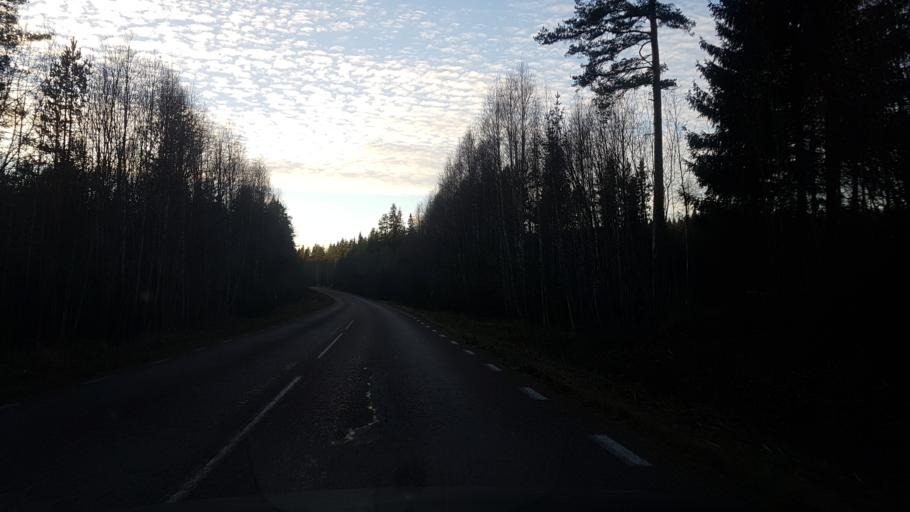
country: SE
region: Dalarna
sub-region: Leksand Municipality
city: Smedby
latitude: 60.7450
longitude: 15.2118
